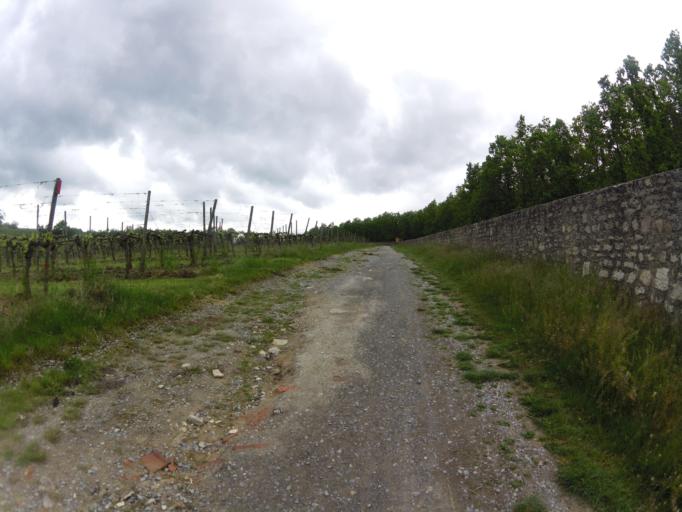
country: DE
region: Bavaria
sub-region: Regierungsbezirk Unterfranken
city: Sommerach
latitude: 49.8507
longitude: 10.2092
